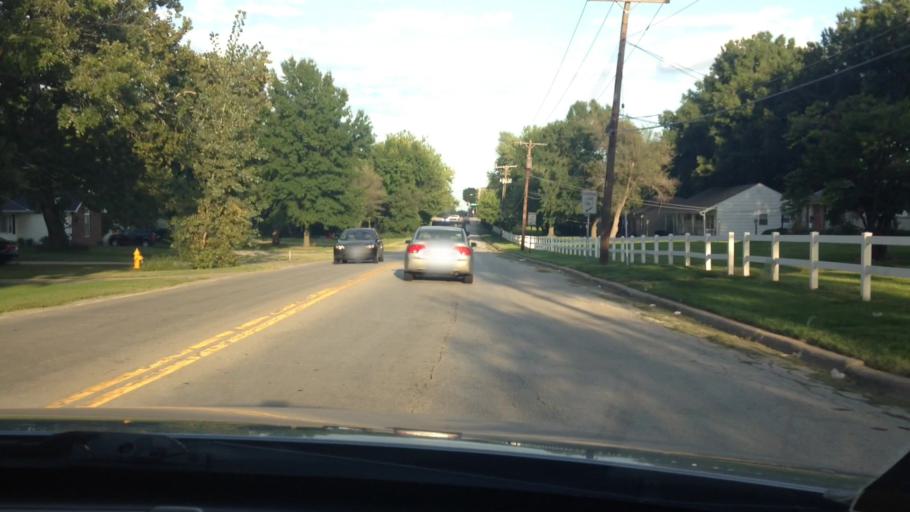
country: US
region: Missouri
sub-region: Jackson County
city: Raytown
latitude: 38.9663
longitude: -94.4972
